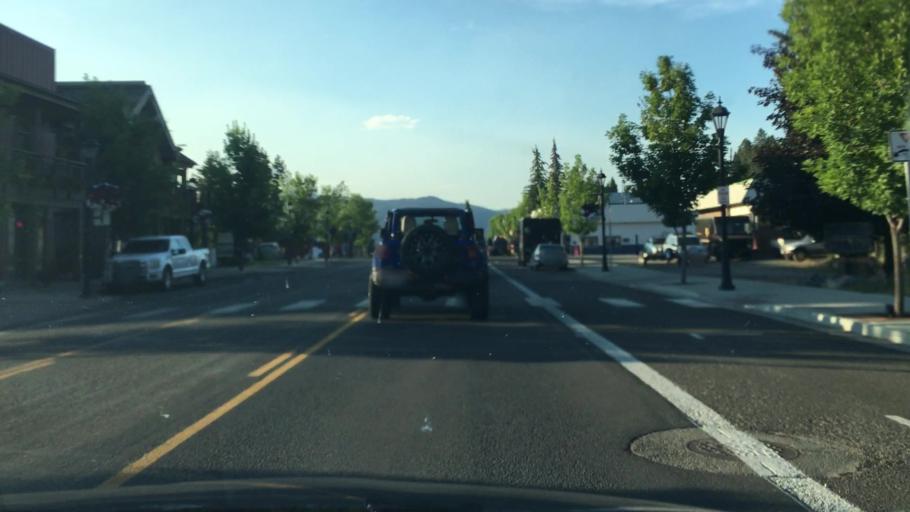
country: US
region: Idaho
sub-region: Valley County
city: McCall
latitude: 44.9074
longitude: -116.0975
